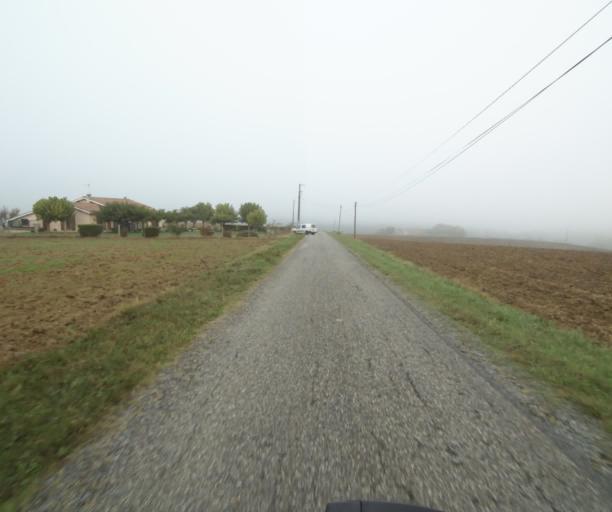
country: FR
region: Midi-Pyrenees
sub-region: Departement du Tarn-et-Garonne
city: Nohic
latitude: 43.9269
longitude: 1.4790
